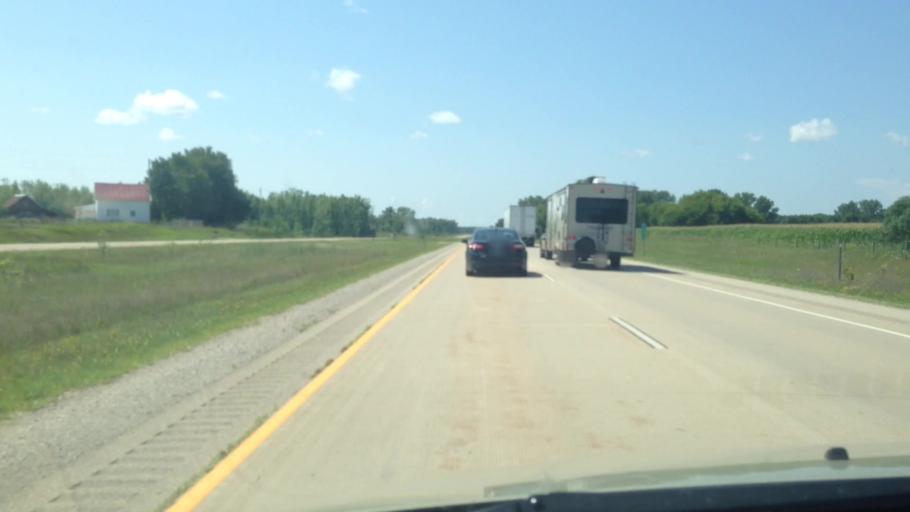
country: US
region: Wisconsin
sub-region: Oconto County
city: Oconto
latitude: 44.9873
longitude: -87.8603
